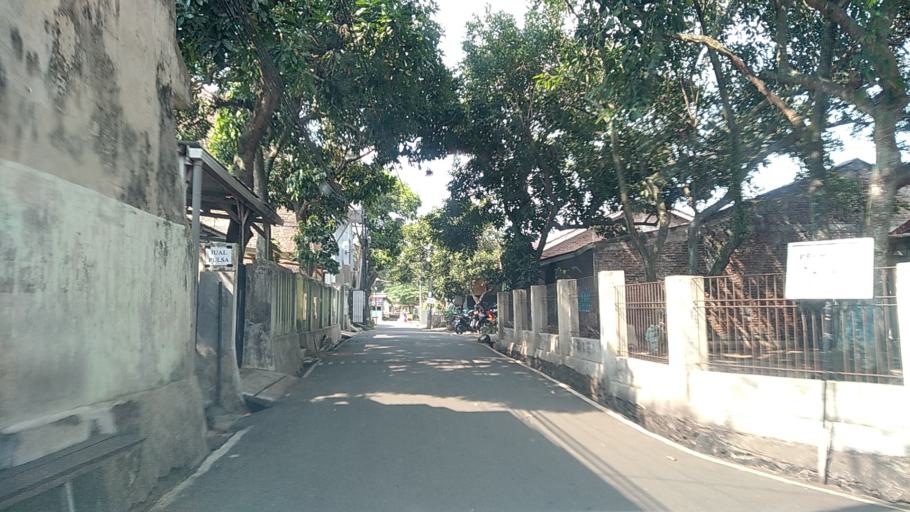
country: ID
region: Central Java
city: Semarang
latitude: -7.0491
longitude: 110.4235
